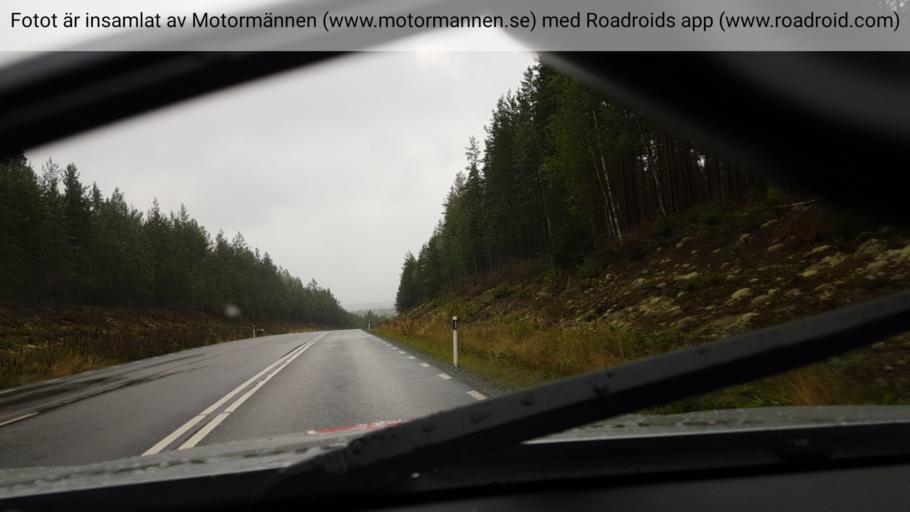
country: SE
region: Vaestra Goetaland
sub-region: Bengtsfors Kommun
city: Dals Langed
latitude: 58.8478
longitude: 12.1680
